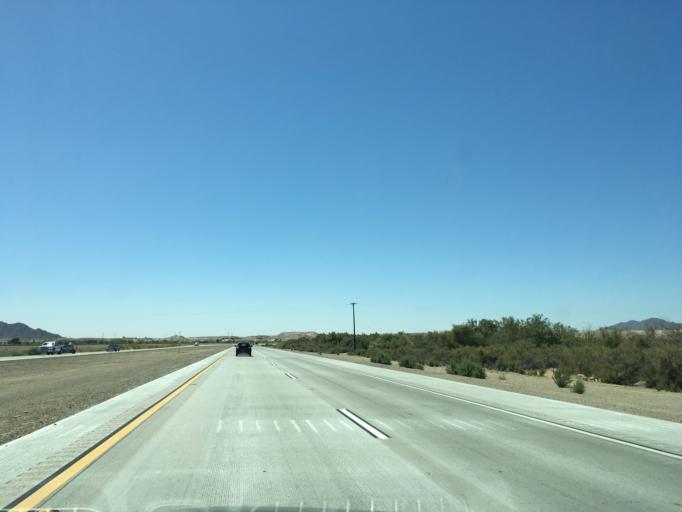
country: US
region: Arizona
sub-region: Yuma County
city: Yuma
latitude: 32.7407
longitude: -114.6791
